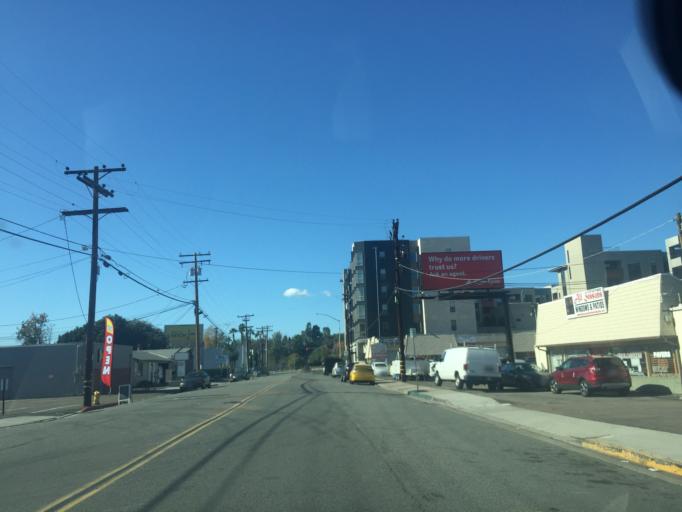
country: US
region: California
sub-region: San Diego County
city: La Mesa
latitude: 32.7851
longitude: -117.0995
